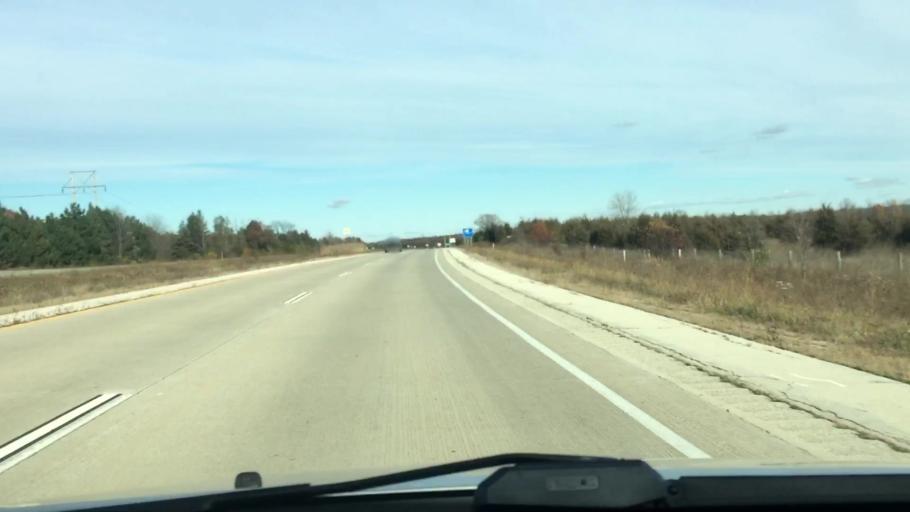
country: US
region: Wisconsin
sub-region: Kewaunee County
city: Luxemburg
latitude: 44.6156
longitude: -87.8311
